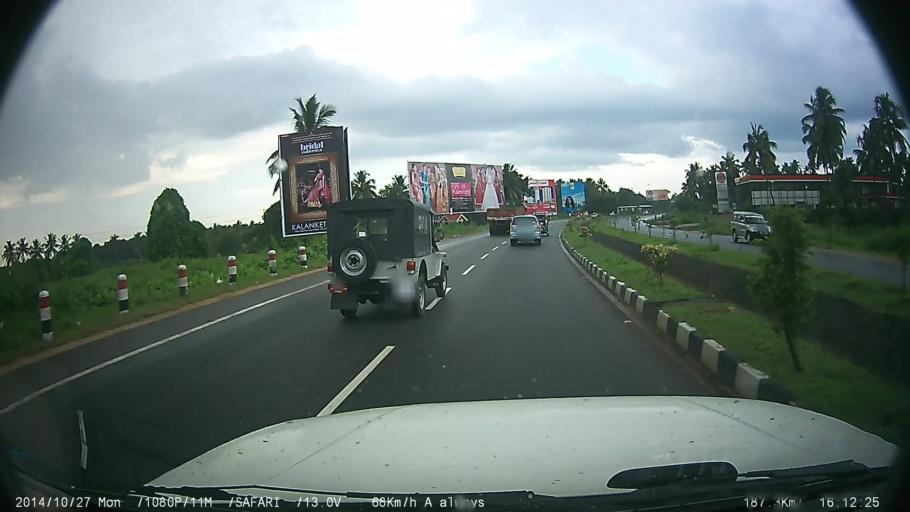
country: IN
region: Kerala
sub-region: Thrissur District
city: Irinjalakuda
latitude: 10.4060
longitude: 76.2758
